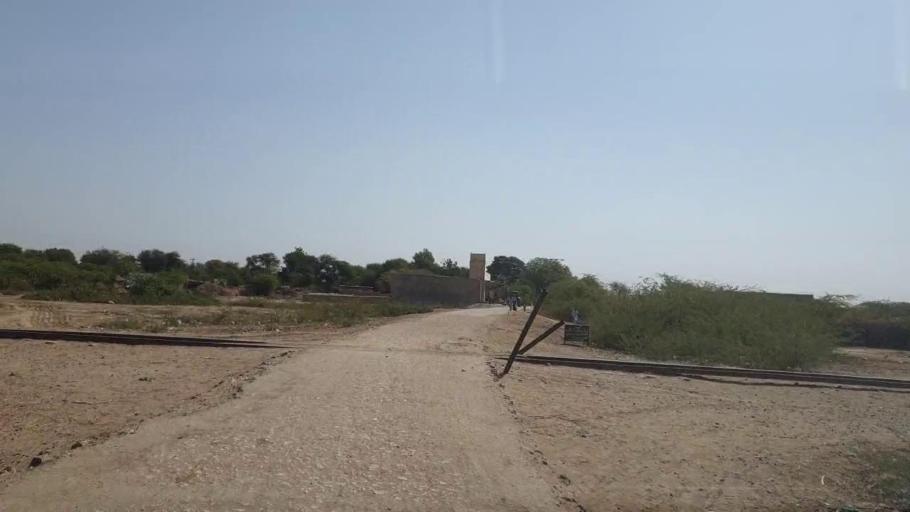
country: PK
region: Sindh
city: Naukot
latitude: 24.9756
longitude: 69.4866
